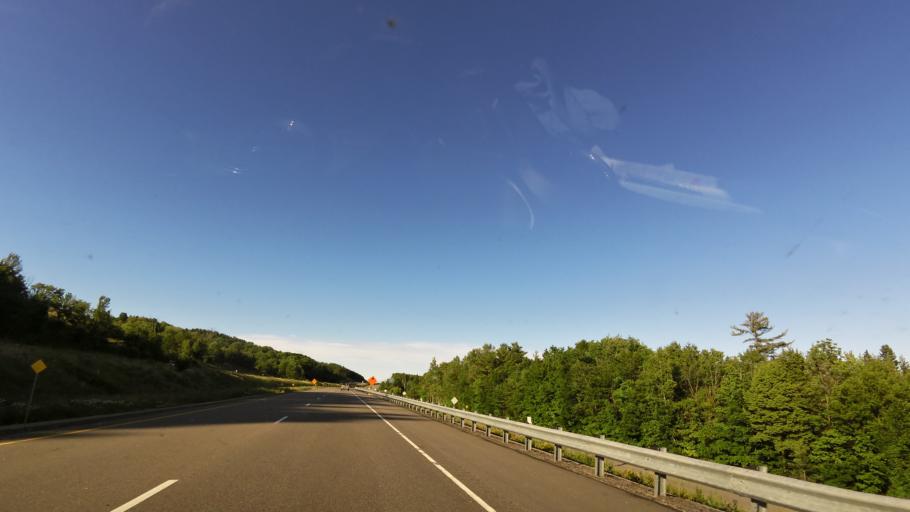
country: CA
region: Ontario
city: Barrie
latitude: 44.5778
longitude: -79.7051
